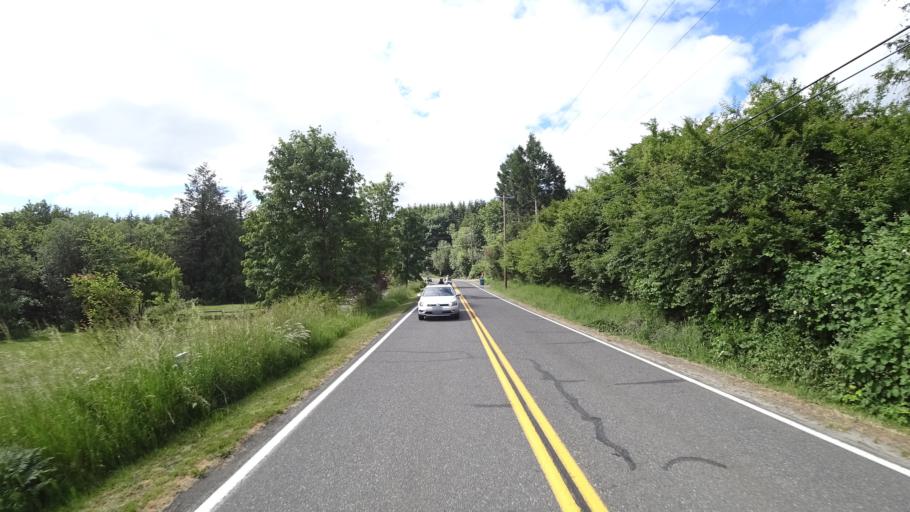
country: US
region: Oregon
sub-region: Washington County
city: Bethany
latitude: 45.6067
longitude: -122.8344
